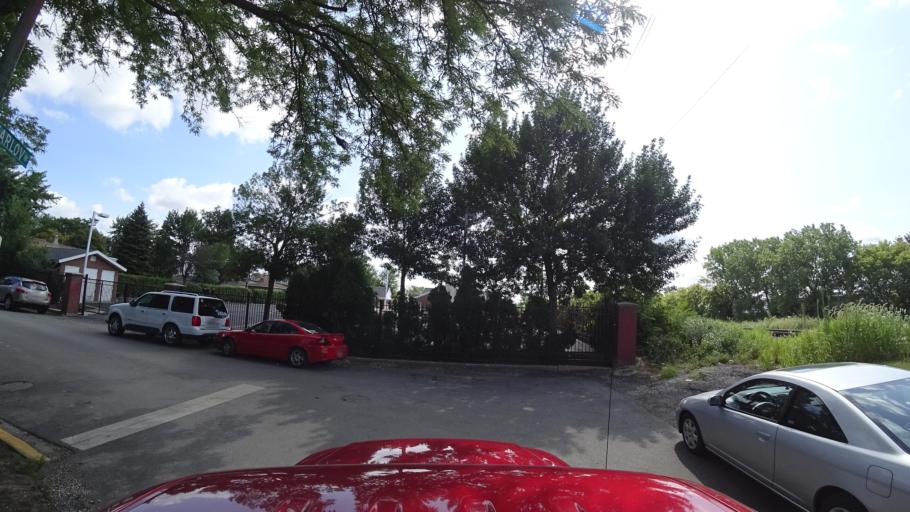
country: US
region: Illinois
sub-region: Cook County
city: Cicero
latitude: 41.8332
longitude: -87.7268
